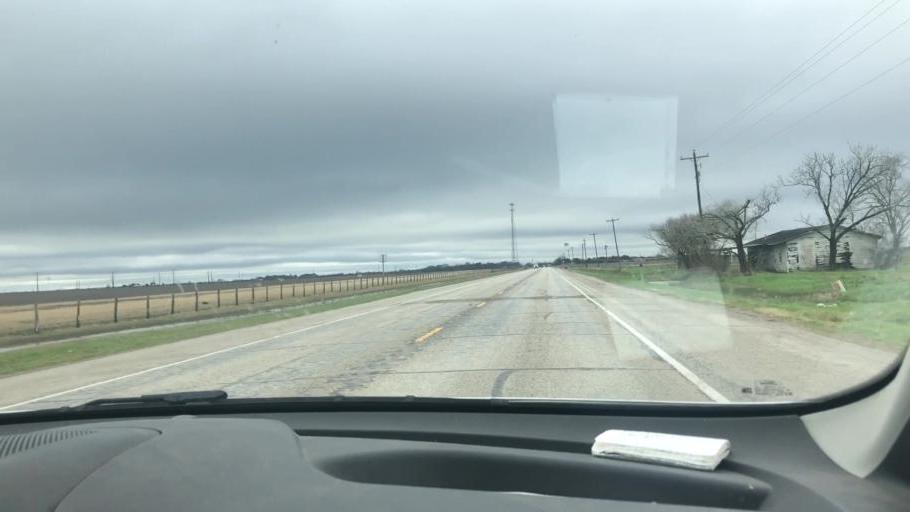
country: US
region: Texas
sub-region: Wharton County
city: Wharton
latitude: 29.2383
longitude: -96.0393
